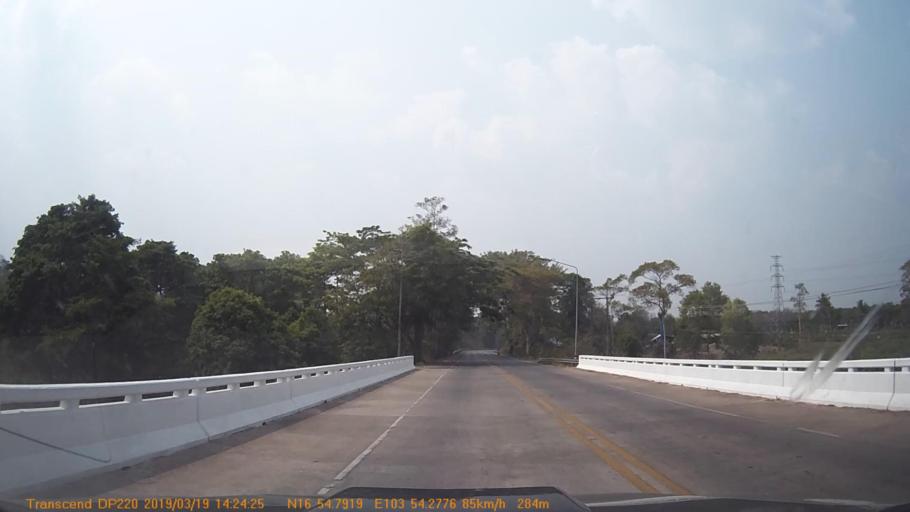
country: TH
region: Sakon Nakhon
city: Phu Phan
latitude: 16.9137
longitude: 103.9043
